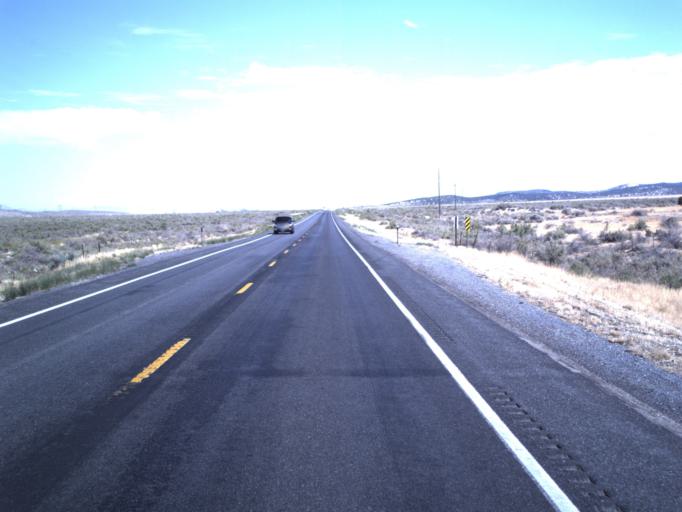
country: US
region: Utah
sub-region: Sanpete County
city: Gunnison
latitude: 39.2916
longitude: -111.8873
